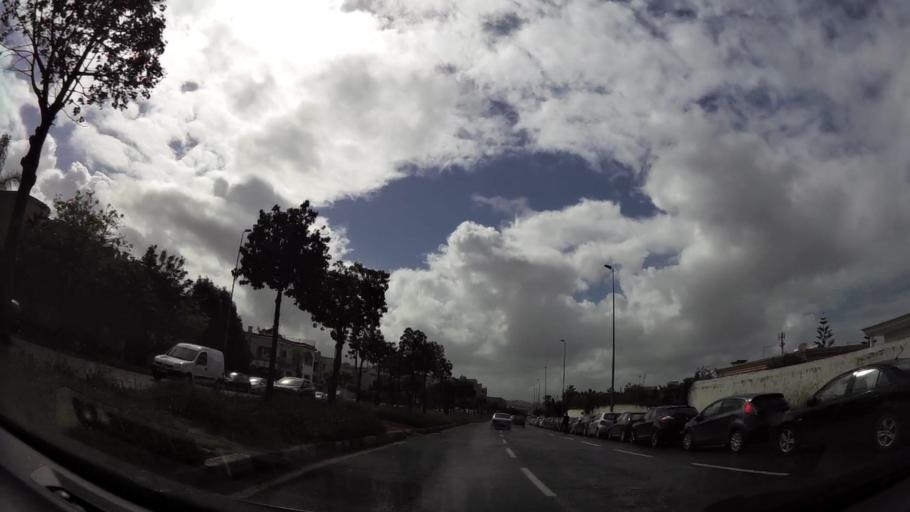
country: MA
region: Grand Casablanca
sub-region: Casablanca
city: Casablanca
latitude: 33.5303
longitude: -7.6423
